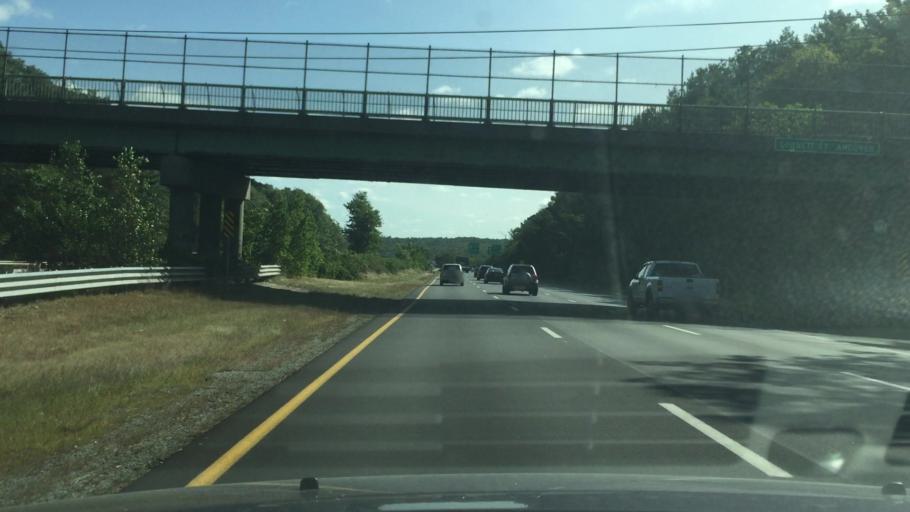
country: US
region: Massachusetts
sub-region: Essex County
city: Lawrence
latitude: 42.6770
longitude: -71.1609
